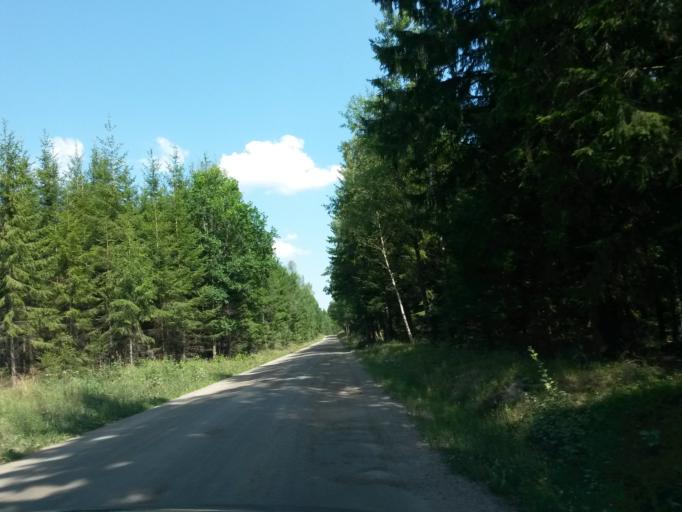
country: SE
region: Vaestra Goetaland
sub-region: Vargarda Kommun
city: Vargarda
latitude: 58.0413
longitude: 12.8864
